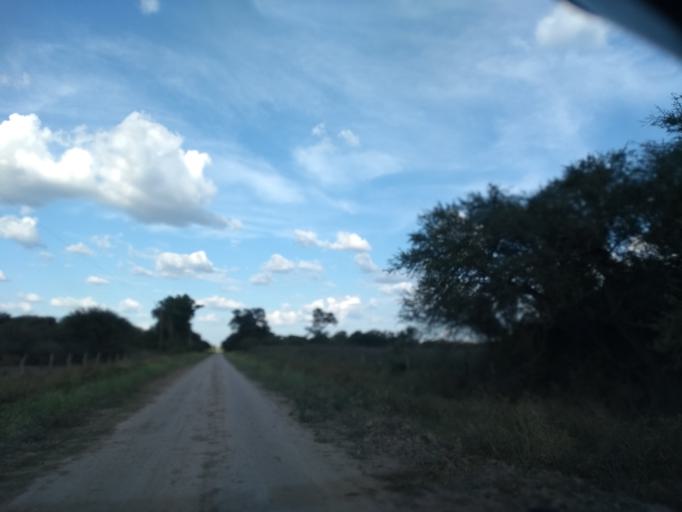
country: AR
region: Chaco
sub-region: Departamento de Quitilipi
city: Quitilipi
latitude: -26.7559
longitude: -60.2462
